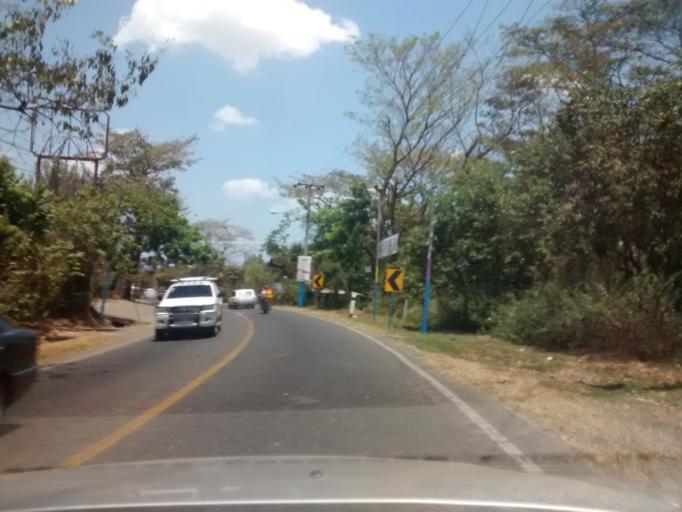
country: NI
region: Masaya
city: Ticuantepe
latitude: 12.0446
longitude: -86.2018
